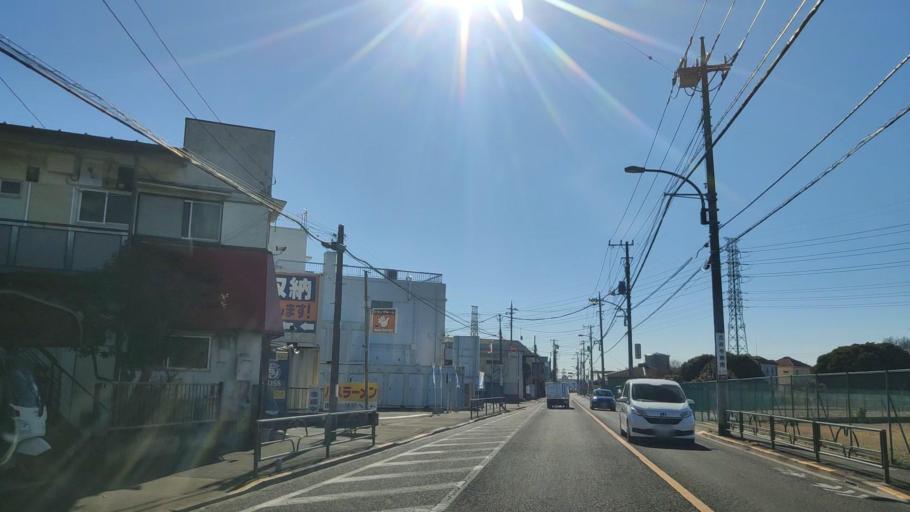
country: JP
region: Tokyo
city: Mitaka-shi
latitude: 35.6742
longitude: 139.5546
